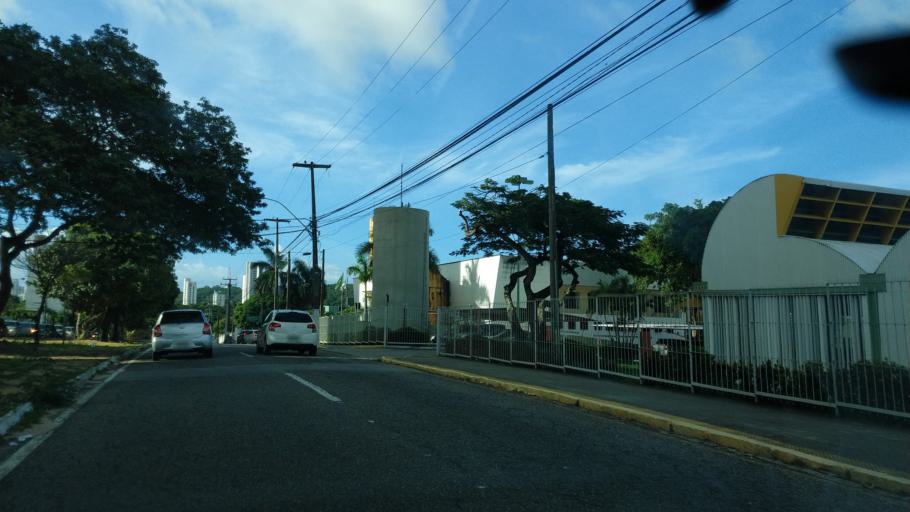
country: BR
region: Rio Grande do Norte
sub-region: Natal
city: Natal
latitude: -5.8106
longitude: -35.2011
